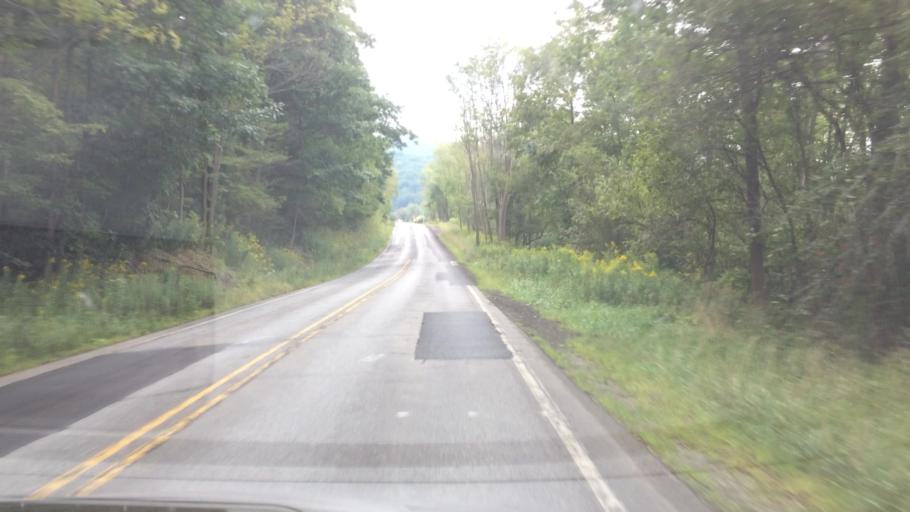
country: US
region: Pennsylvania
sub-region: McKean County
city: Bradford
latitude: 41.9185
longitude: -78.6438
